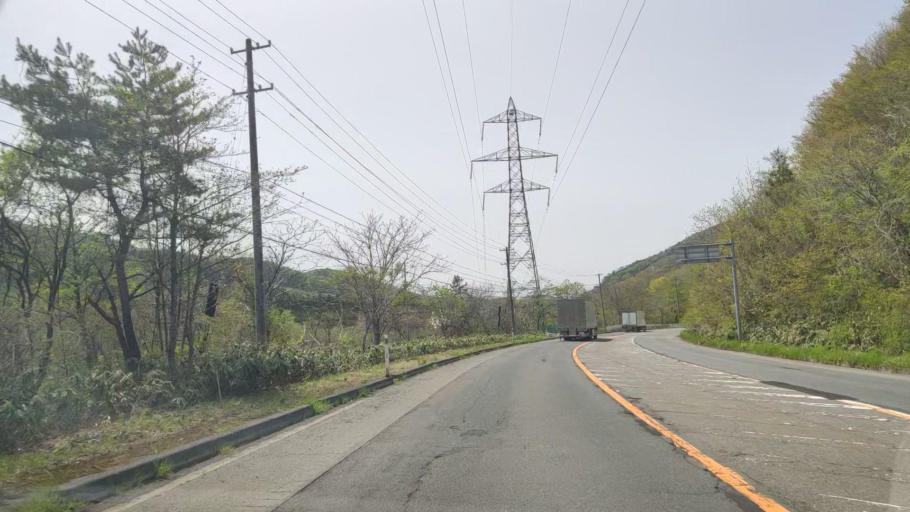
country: JP
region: Aomori
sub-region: Misawa Shi
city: Inuotose
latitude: 40.7907
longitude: 141.0985
